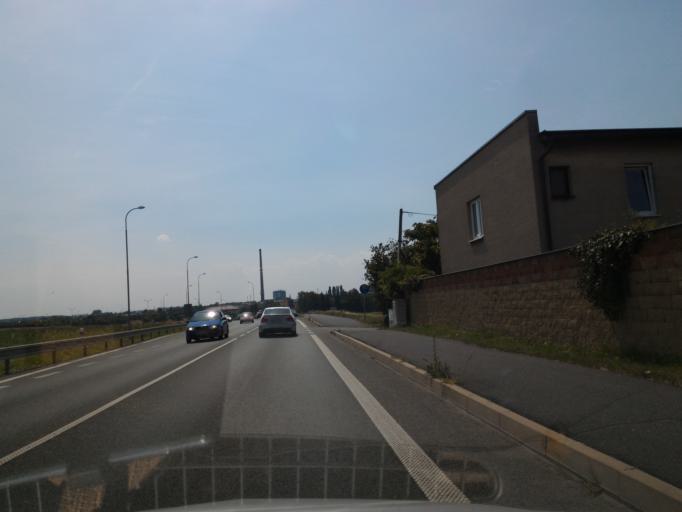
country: CZ
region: Central Bohemia
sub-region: Okres Nymburk
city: Nymburk
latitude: 50.2066
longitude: 15.0349
